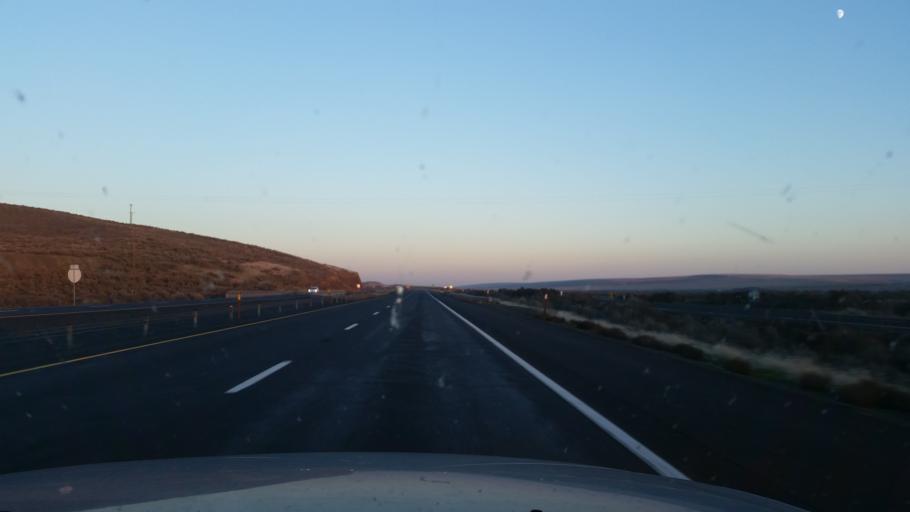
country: US
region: Washington
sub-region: Grant County
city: Warden
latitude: 47.0845
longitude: -118.9873
